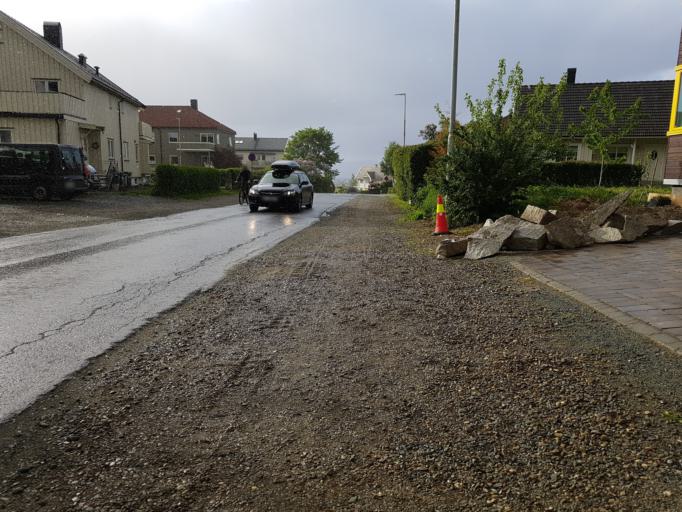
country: NO
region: Sor-Trondelag
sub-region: Trondheim
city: Trondheim
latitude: 63.4338
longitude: 10.4404
